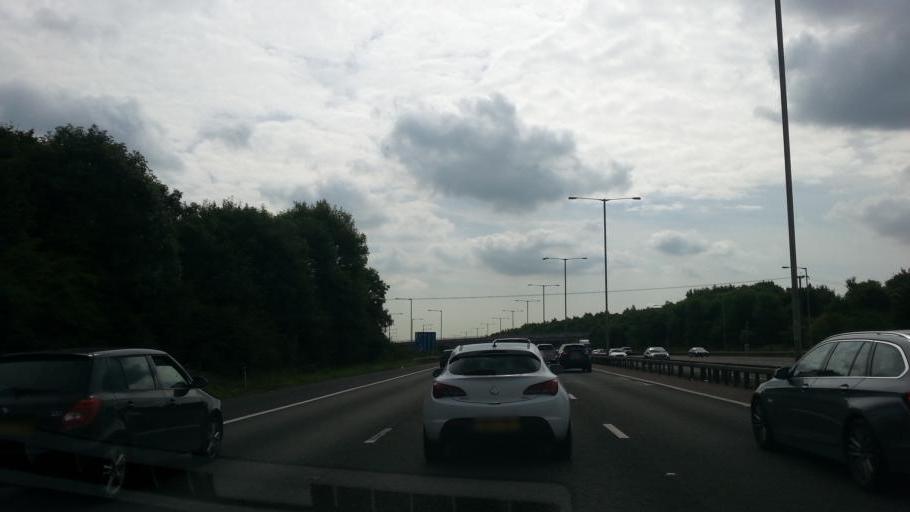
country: GB
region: England
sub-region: Buckinghamshire
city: Denham
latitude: 51.5554
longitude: -0.5279
